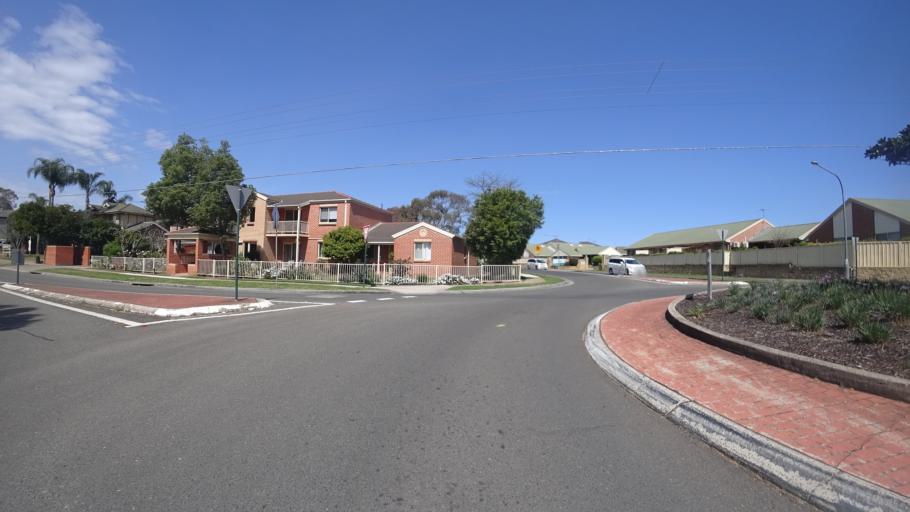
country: AU
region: New South Wales
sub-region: Campbelltown Municipality
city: Glenfield
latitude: -33.9530
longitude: 150.8954
